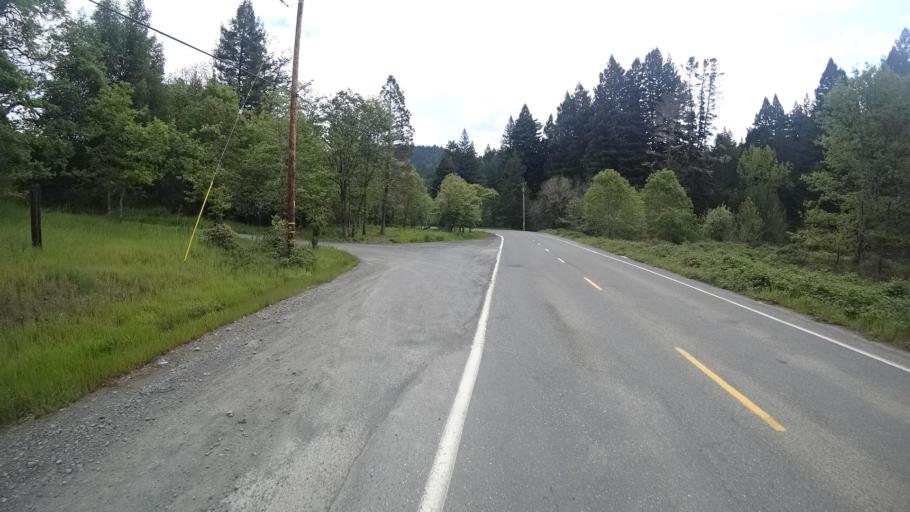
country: US
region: California
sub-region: Humboldt County
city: Redway
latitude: 40.1106
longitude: -123.8926
